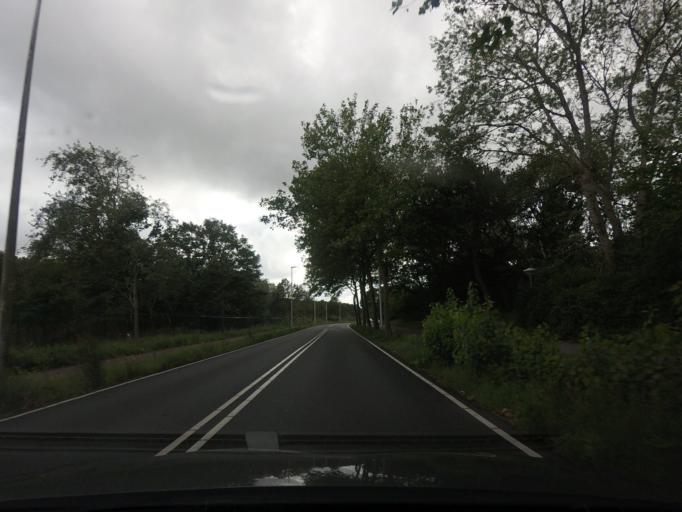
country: NL
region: North Holland
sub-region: Gemeente Zandvoort
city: Zandvoort
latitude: 52.3656
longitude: 4.5596
